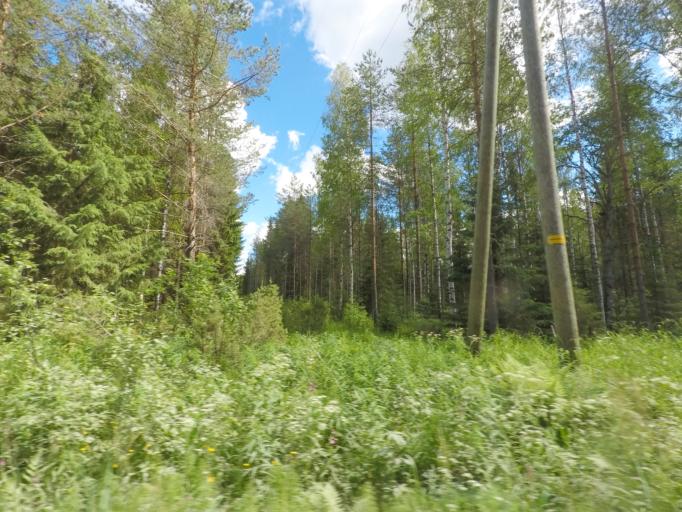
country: FI
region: Central Finland
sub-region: Jyvaeskylae
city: Hankasalmi
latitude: 62.4353
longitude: 26.6477
